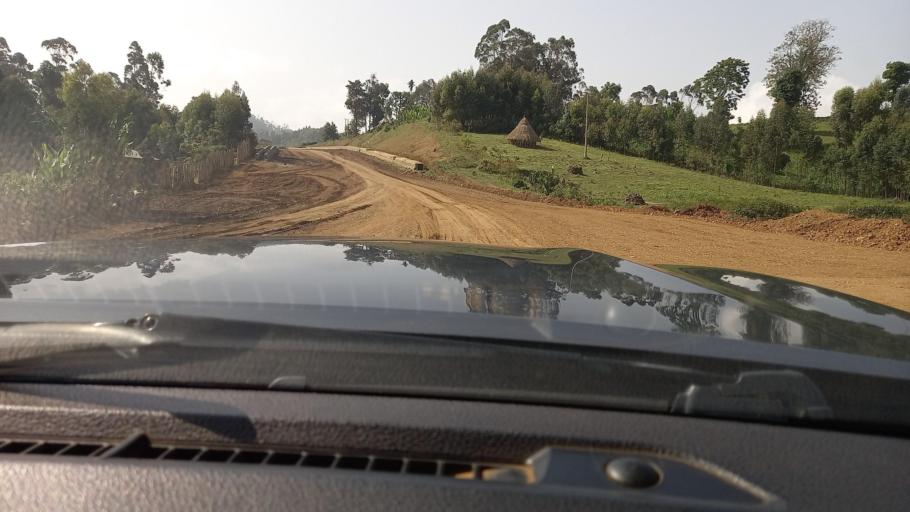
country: ET
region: Southern Nations, Nationalities, and People's Region
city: Mizan Teferi
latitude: 6.1680
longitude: 35.5849
